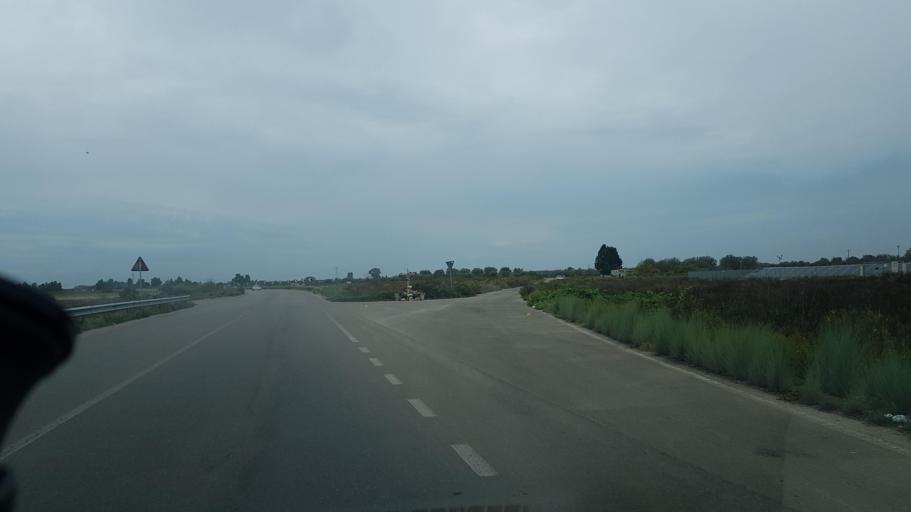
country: IT
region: Apulia
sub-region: Provincia di Lecce
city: Carmiano
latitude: 40.3137
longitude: 18.0393
